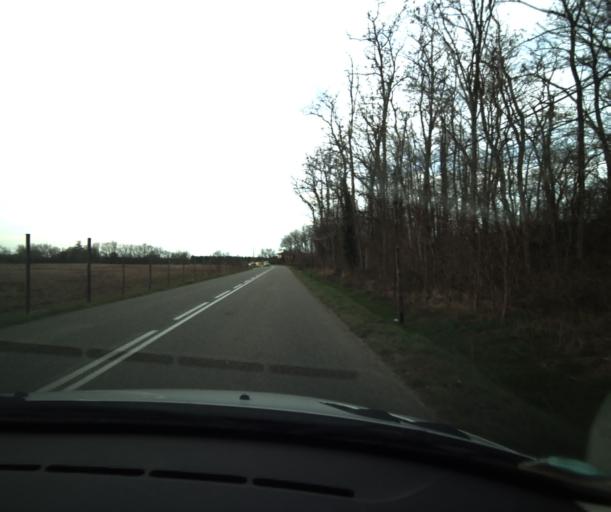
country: FR
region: Midi-Pyrenees
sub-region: Departement du Tarn-et-Garonne
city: Finhan
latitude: 43.9281
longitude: 1.2563
